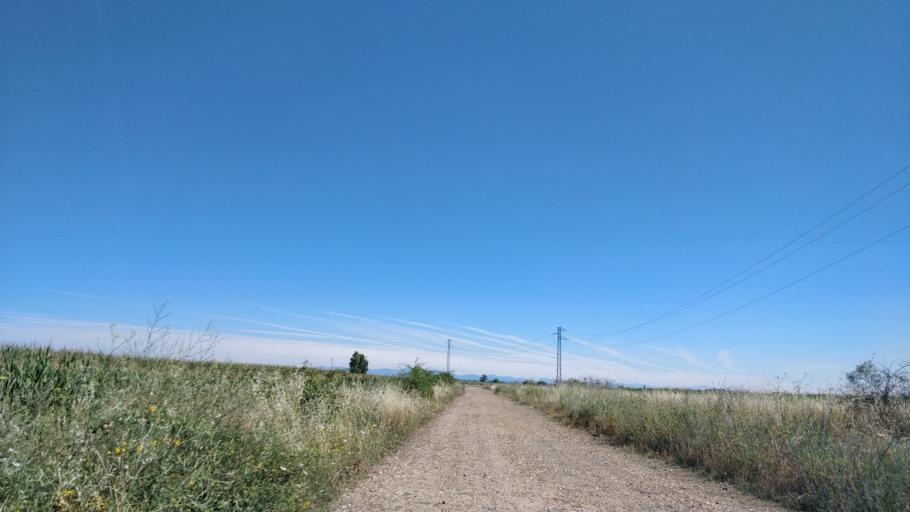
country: ES
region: Castille and Leon
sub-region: Provincia de Leon
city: Bustillo del Paramo
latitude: 42.4369
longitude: -5.8210
